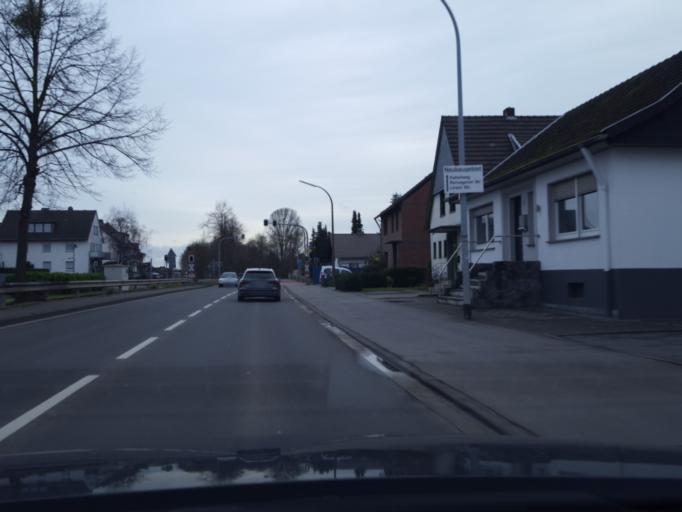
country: DE
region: North Rhine-Westphalia
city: Niederkassel
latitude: 50.7907
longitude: 7.0543
